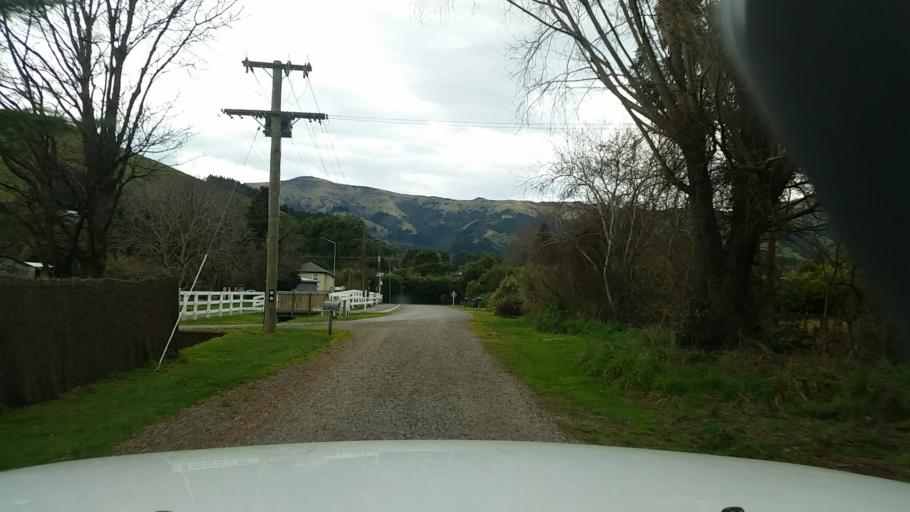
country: NZ
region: Canterbury
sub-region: Christchurch City
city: Christchurch
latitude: -43.7725
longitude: 172.7880
